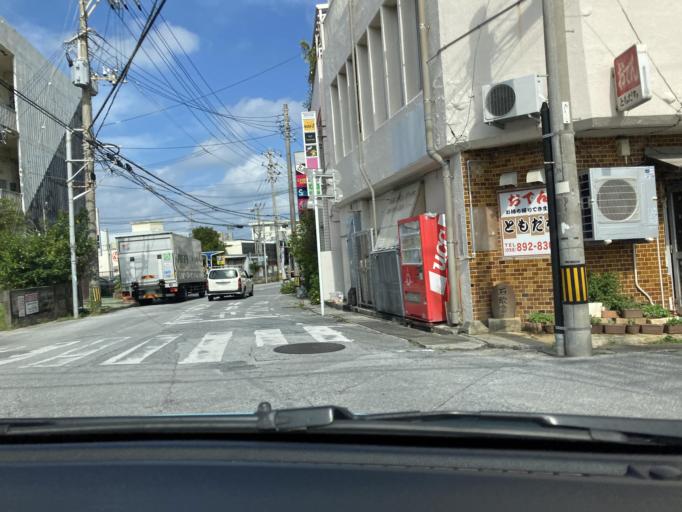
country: JP
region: Okinawa
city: Chatan
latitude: 26.2909
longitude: 127.7766
